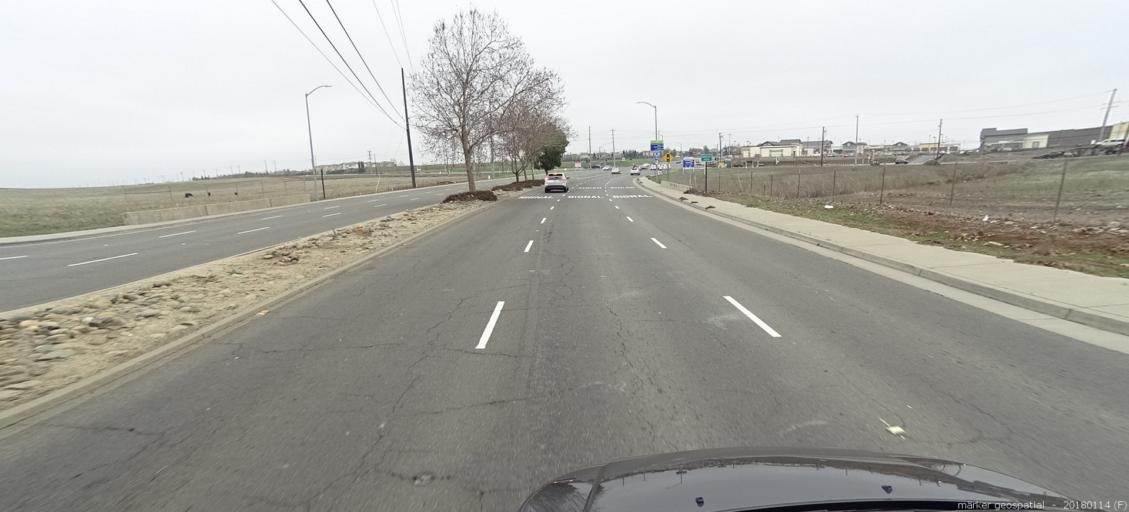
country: US
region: California
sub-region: Sacramento County
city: Rancho Cordova
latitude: 38.5614
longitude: -121.2447
